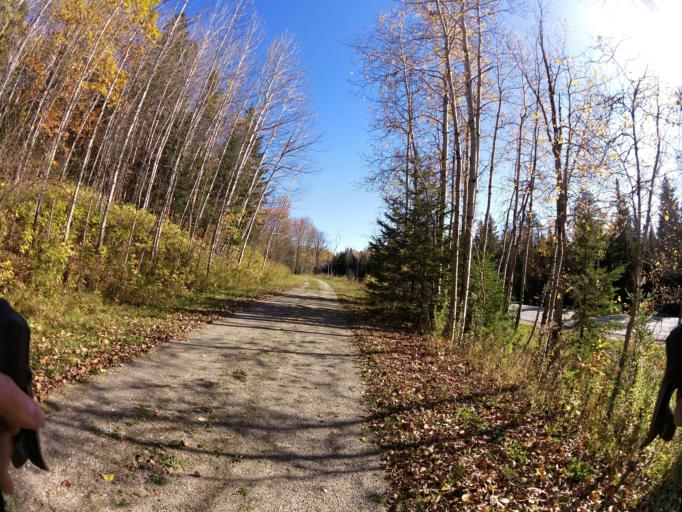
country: CA
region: Quebec
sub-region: Outaouais
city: Wakefield
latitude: 45.8458
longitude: -75.9841
